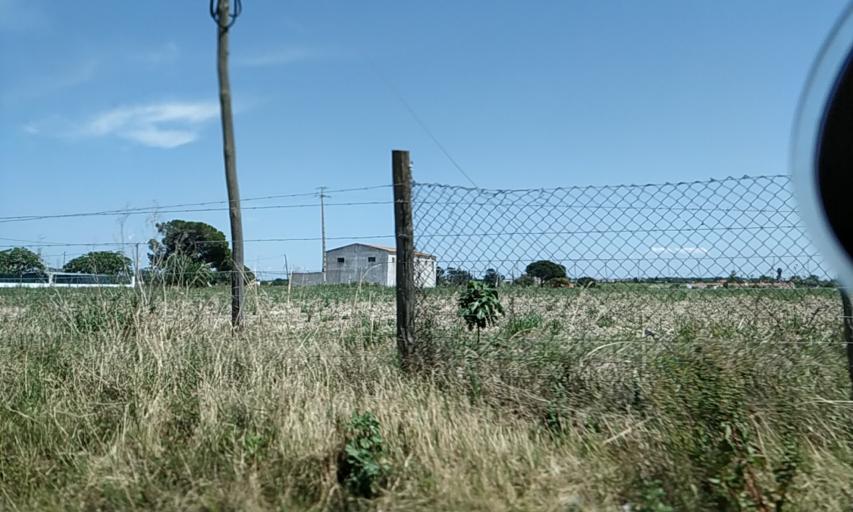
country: PT
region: Santarem
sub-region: Benavente
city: Poceirao
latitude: 38.6794
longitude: -8.7330
